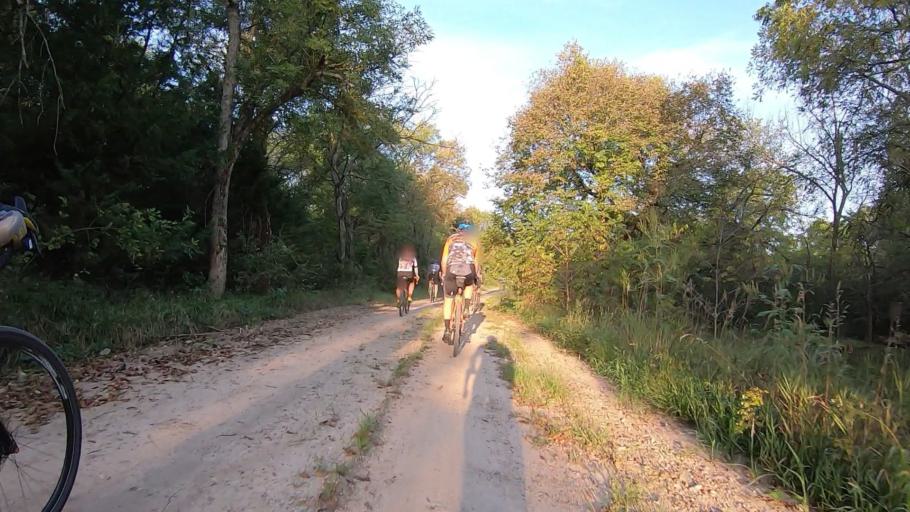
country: US
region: Kansas
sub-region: Marshall County
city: Marysville
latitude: 39.7657
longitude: -96.7024
